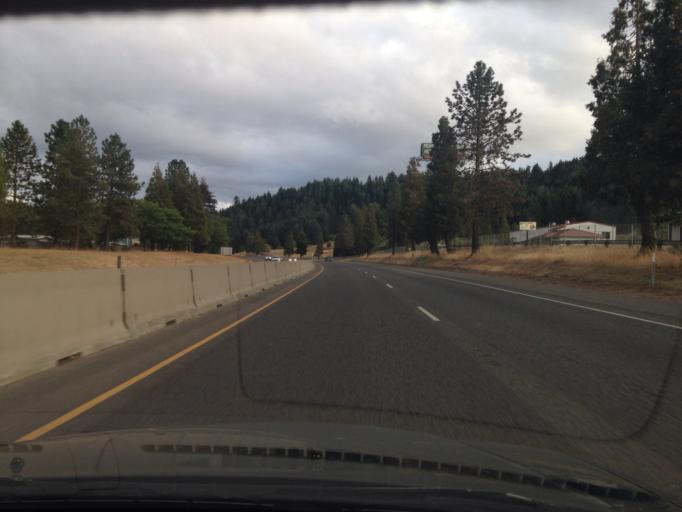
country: US
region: Oregon
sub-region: Douglas County
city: Sutherlin
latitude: 43.3797
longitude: -123.3384
